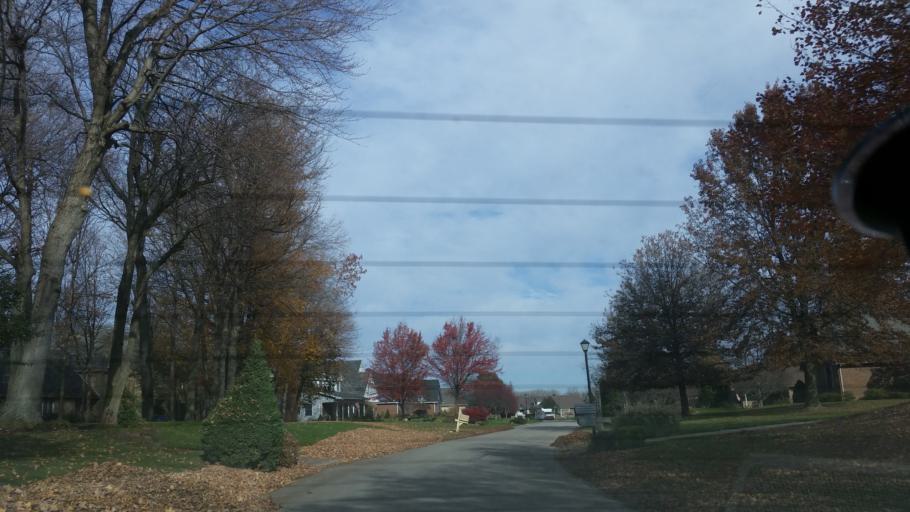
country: US
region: Indiana
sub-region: Howard County
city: Indian Heights
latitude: 40.4282
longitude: -86.1606
